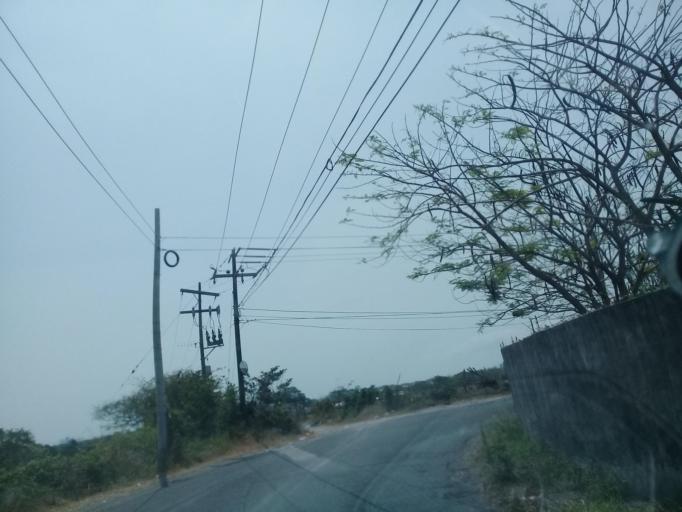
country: MX
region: Veracruz
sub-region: Veracruz
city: Hacienda Sotavento
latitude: 19.1365
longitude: -96.1782
